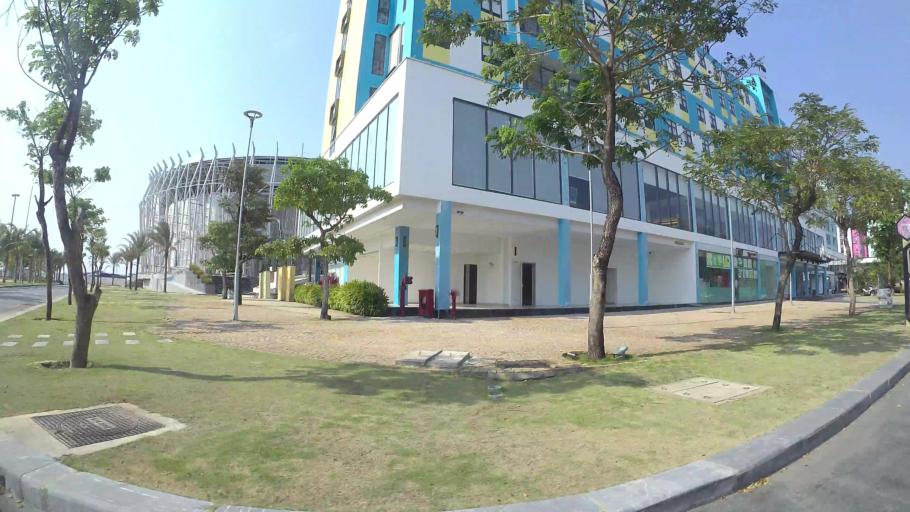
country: VN
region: Da Nang
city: Ngu Hanh Son
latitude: 15.9629
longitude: 108.2790
